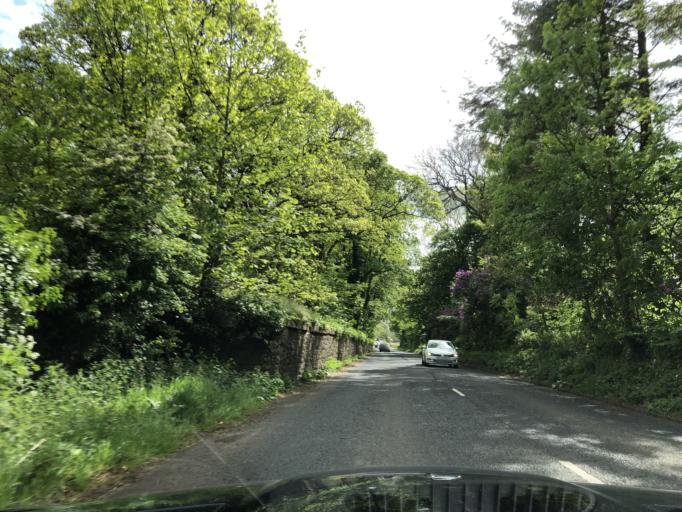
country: GB
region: Northern Ireland
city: Bushmills
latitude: 55.2131
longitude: -6.5188
